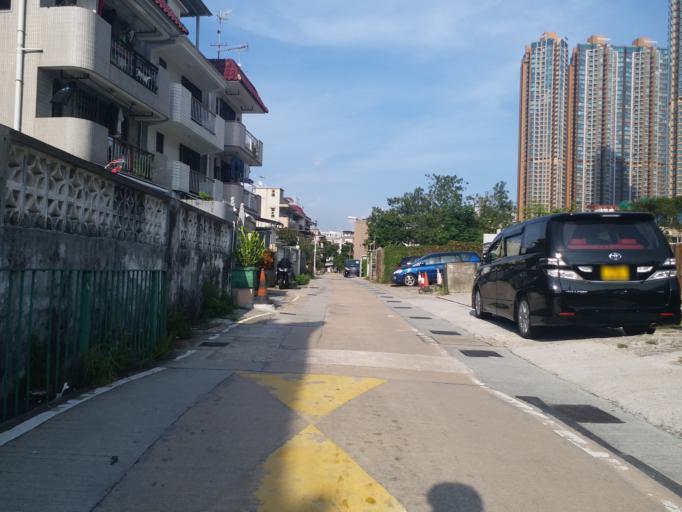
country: HK
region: Yuen Long
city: Yuen Long Kau Hui
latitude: 22.4474
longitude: 114.0349
